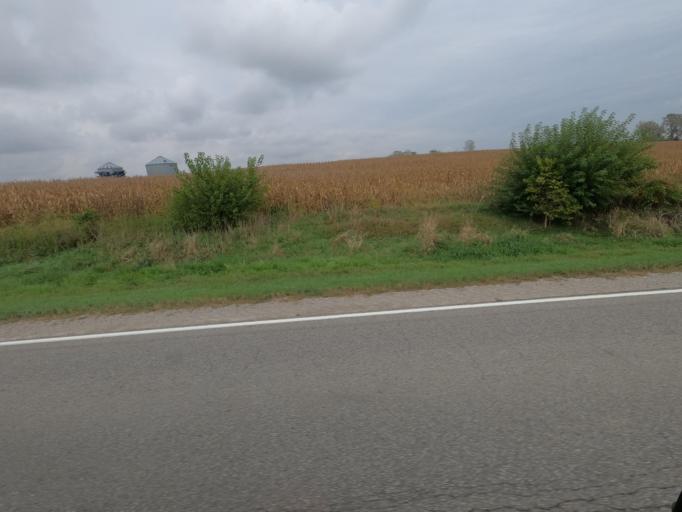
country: US
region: Iowa
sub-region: Wapello County
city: Ottumwa
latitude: 40.9040
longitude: -92.2001
